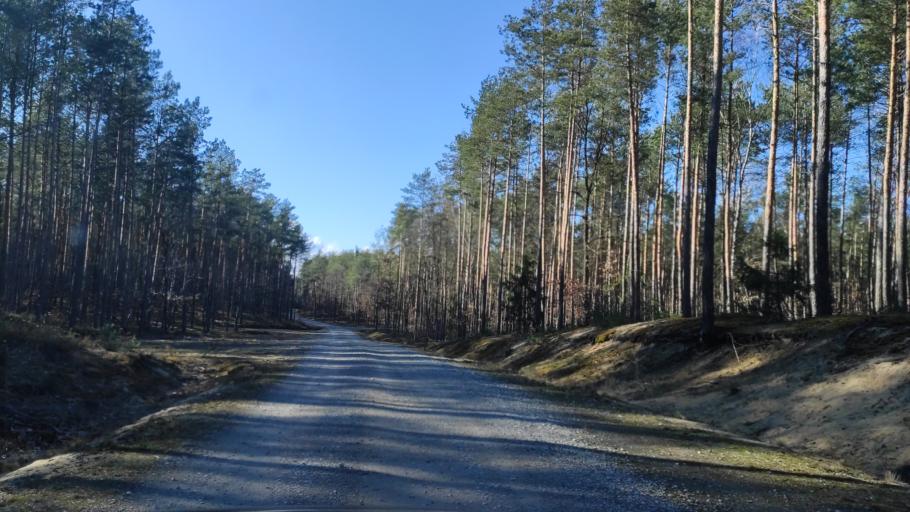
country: PL
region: Masovian Voivodeship
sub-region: Powiat radomski
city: Jastrzebia
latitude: 51.4740
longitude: 21.2916
